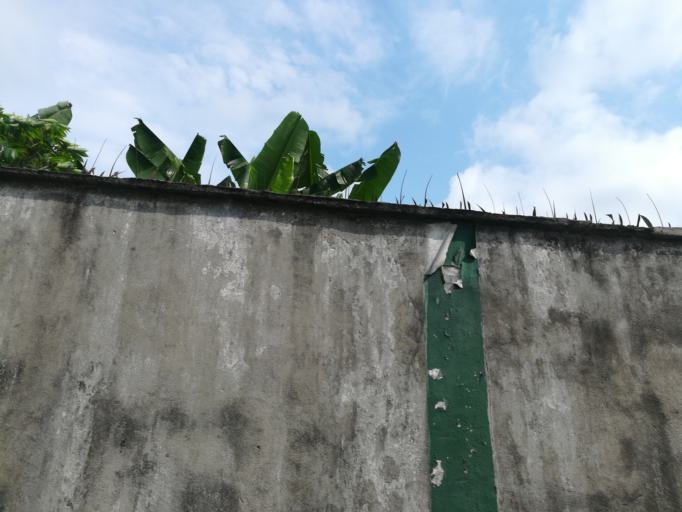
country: NG
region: Rivers
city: Okrika
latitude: 4.7531
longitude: 7.0989
